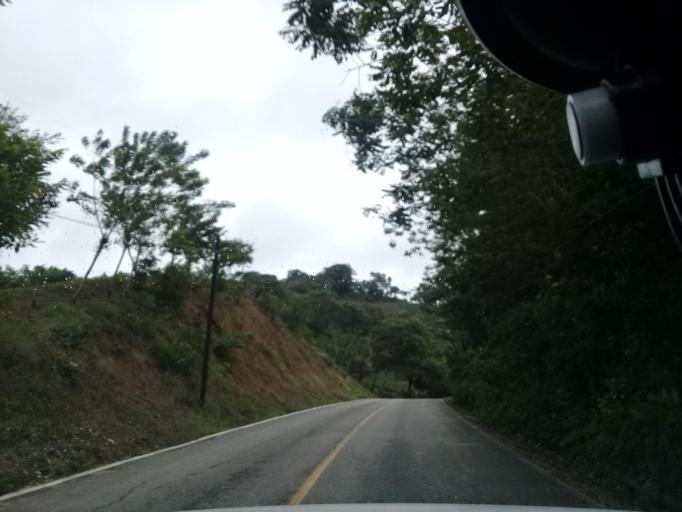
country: MX
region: Veracruz
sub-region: Chalma
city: San Pedro Coyutla
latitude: 21.2152
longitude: -98.4270
